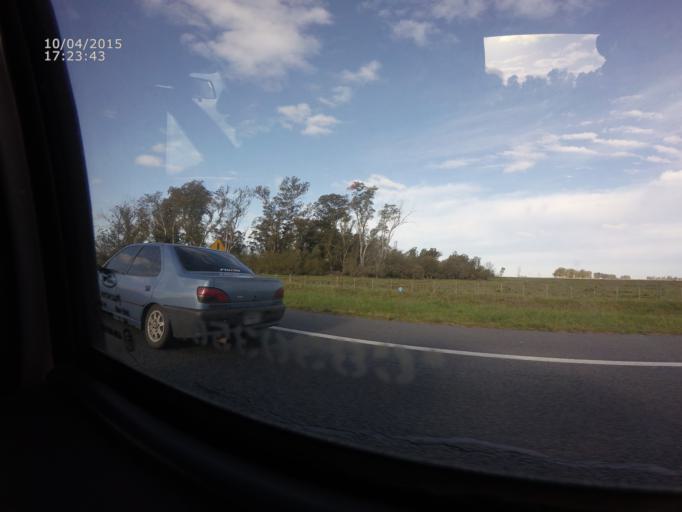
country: AR
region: Buenos Aires
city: Maipu
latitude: -37.0954
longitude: -57.8279
